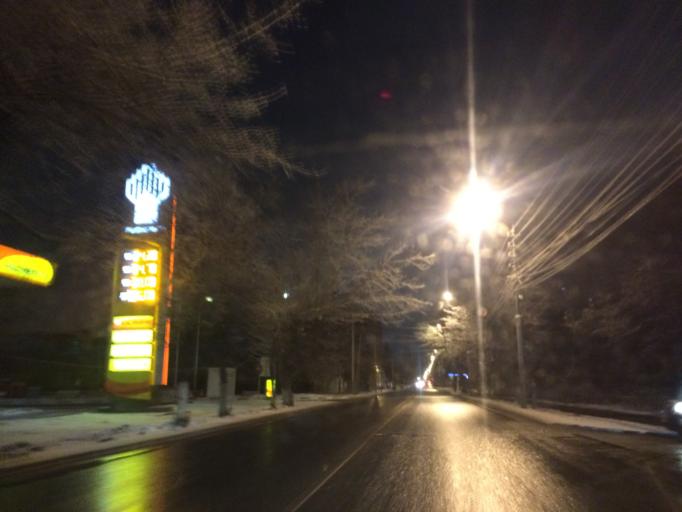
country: RU
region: Tula
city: Tula
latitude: 54.1782
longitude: 37.6302
